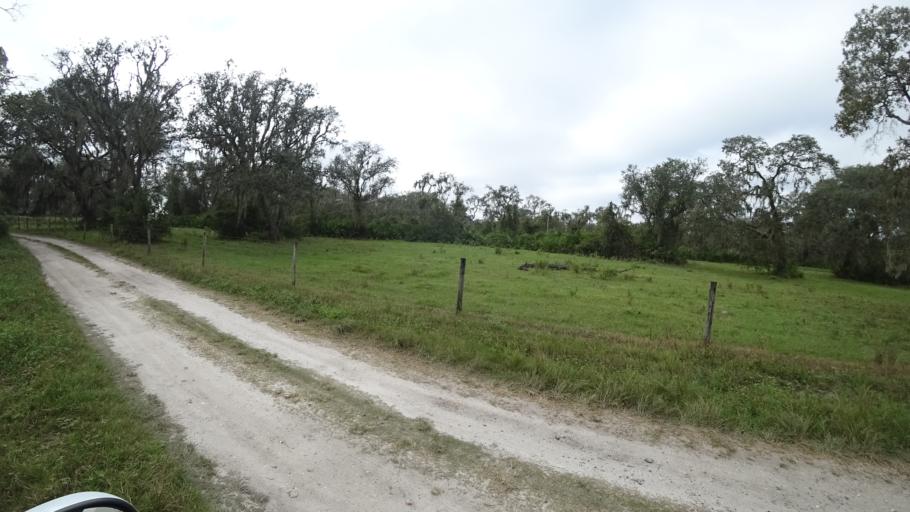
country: US
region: Florida
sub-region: Sarasota County
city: Warm Mineral Springs
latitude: 27.3213
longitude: -82.1379
